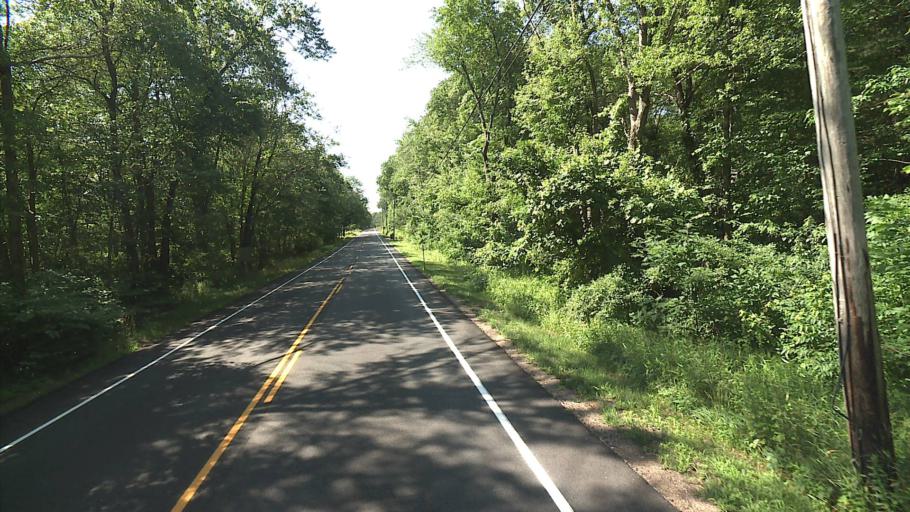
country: US
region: Connecticut
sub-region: Litchfield County
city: Northwest Harwinton
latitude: 41.7555
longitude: -73.0240
